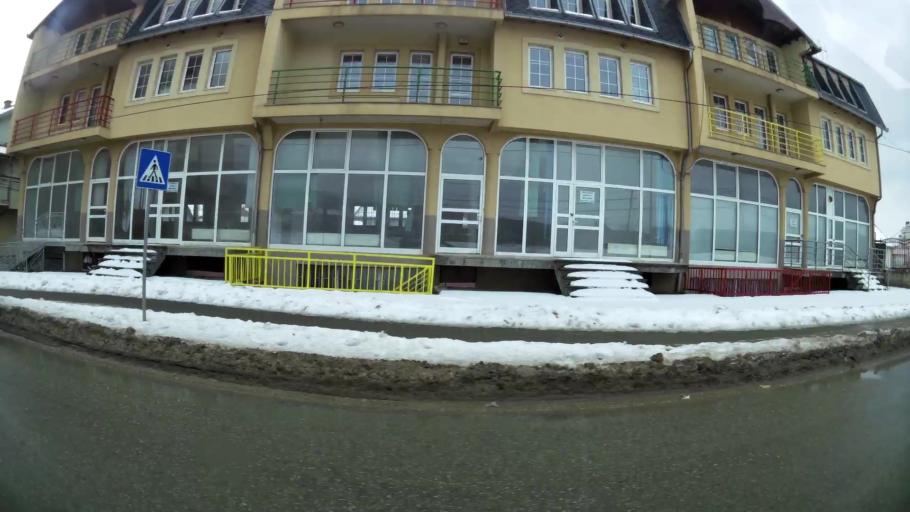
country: XK
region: Pristina
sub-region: Komuna e Prishtines
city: Pristina
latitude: 42.6551
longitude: 21.1896
